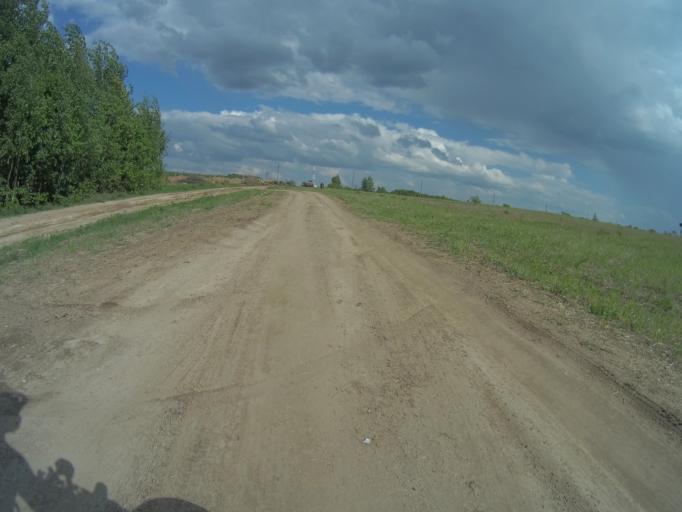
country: RU
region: Vladimir
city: Kommunar
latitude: 56.0725
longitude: 40.4878
